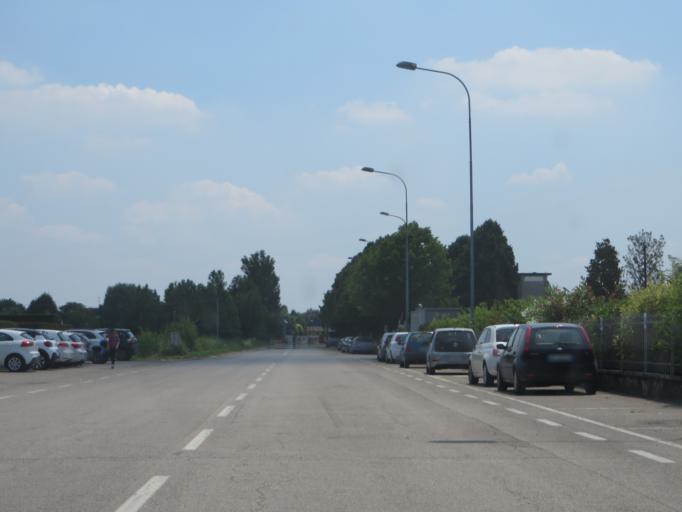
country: IT
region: Veneto
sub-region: Provincia di Verona
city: San Pietro di Morubio
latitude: 45.2301
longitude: 11.2431
